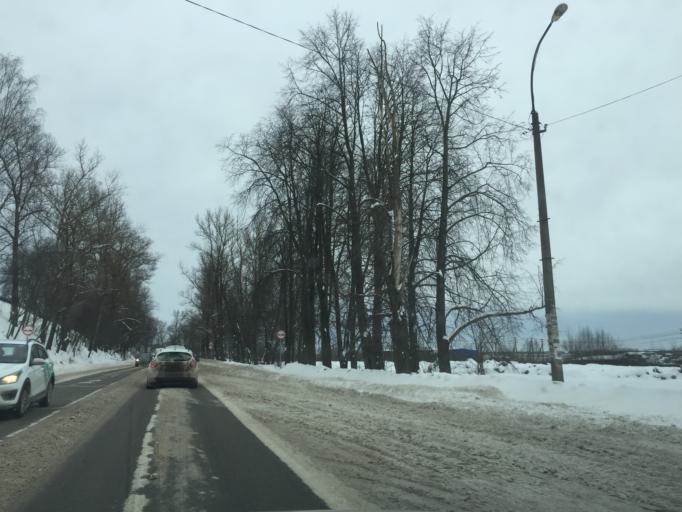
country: RU
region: Leningrad
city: Yanino Vtoroye
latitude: 59.9334
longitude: 30.6133
